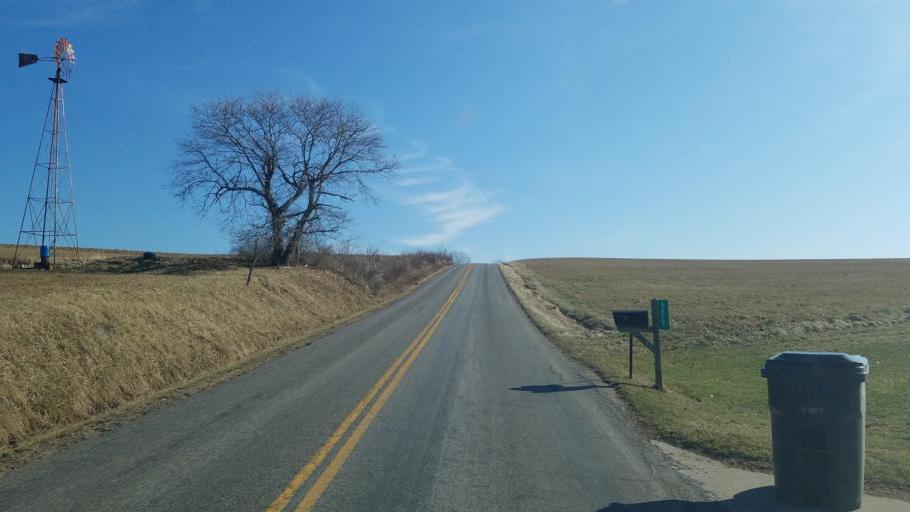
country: US
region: Ohio
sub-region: Holmes County
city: Millersburg
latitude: 40.5727
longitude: -81.8621
